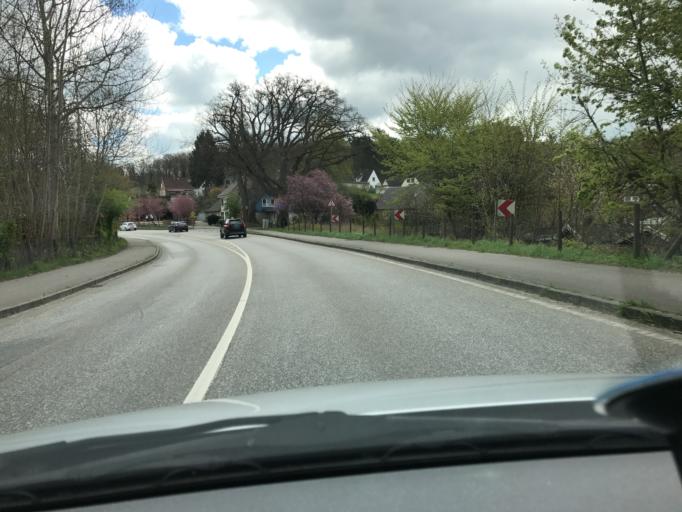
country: DE
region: Schleswig-Holstein
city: Bosdorf
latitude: 54.1468
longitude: 10.4540
